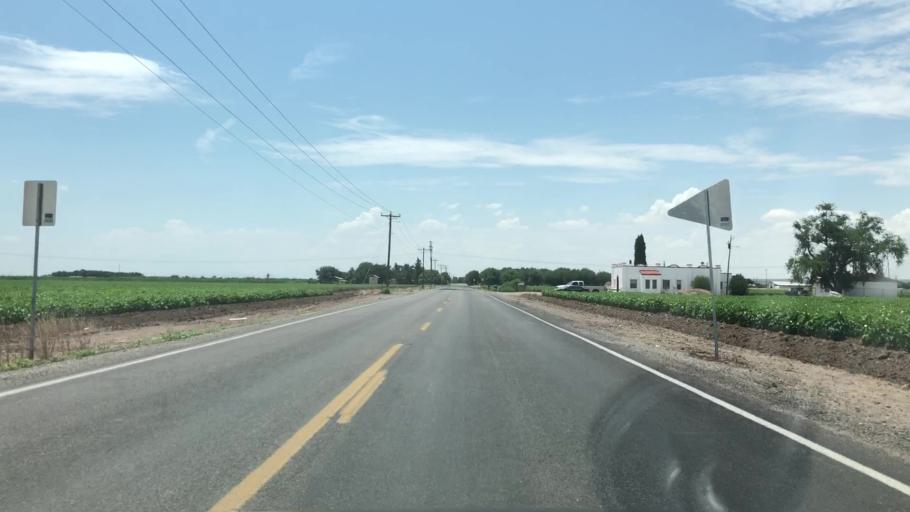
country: US
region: New Mexico
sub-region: Dona Ana County
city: Vado
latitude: 32.1015
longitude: -106.6836
